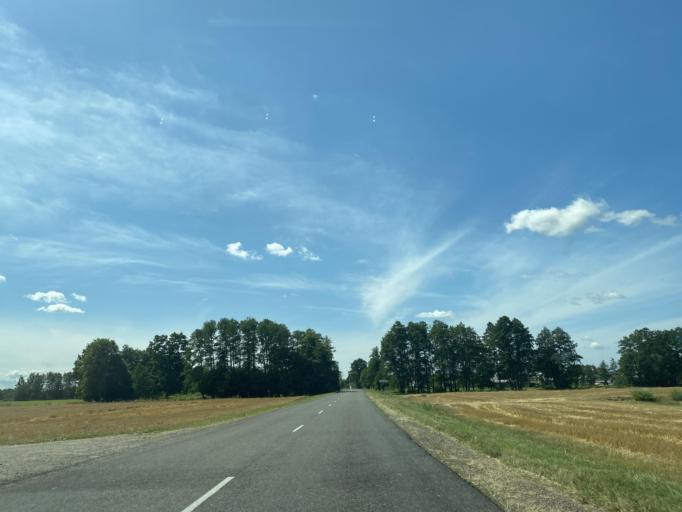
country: BY
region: Brest
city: Ivanava
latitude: 52.1920
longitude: 25.6111
